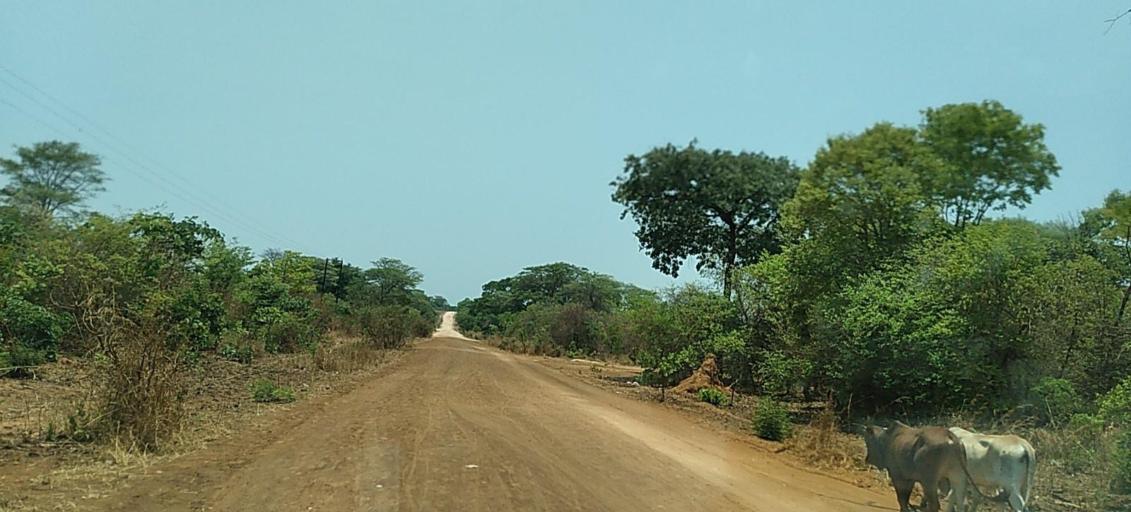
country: ZM
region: Copperbelt
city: Mpongwe
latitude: -13.8164
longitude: 27.8462
